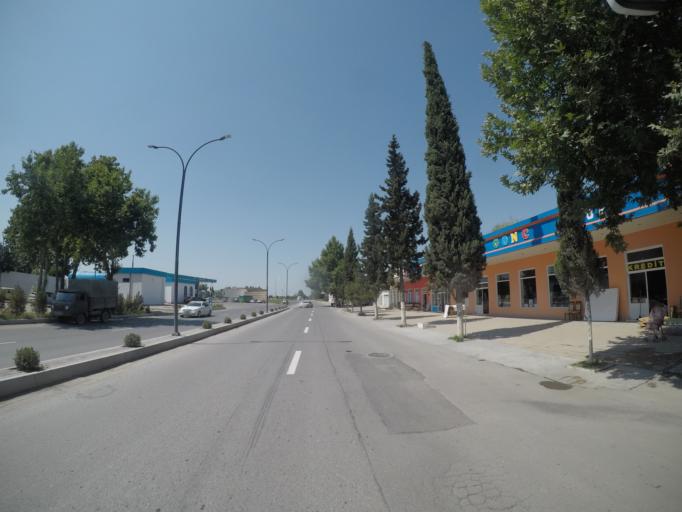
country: AZ
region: Agdas
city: Agdas
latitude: 40.6451
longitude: 47.4952
